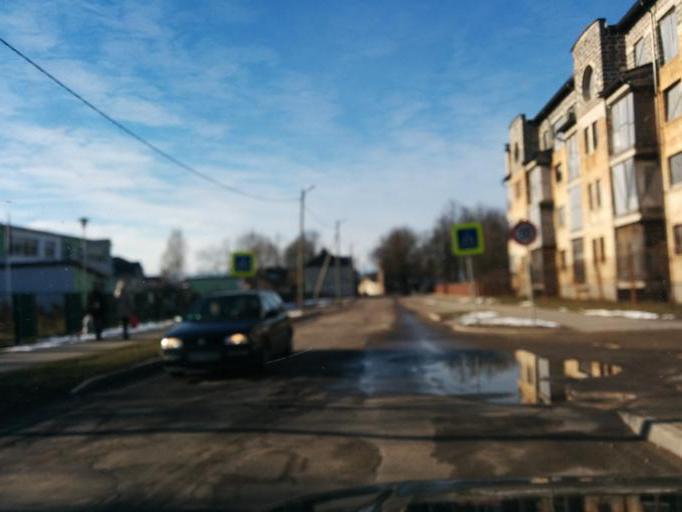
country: LV
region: Jelgava
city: Jelgava
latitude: 56.6543
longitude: 23.7139
